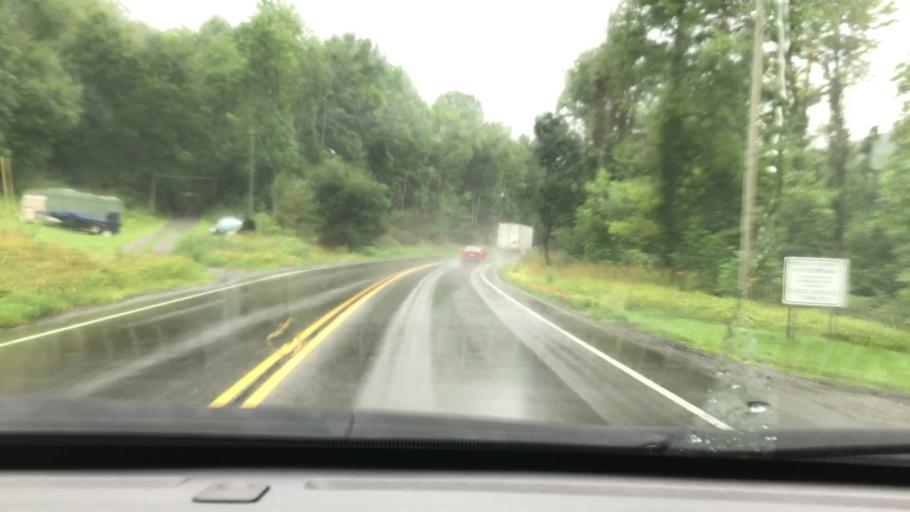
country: US
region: Pennsylvania
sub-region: Blair County
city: Tyrone
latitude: 40.7515
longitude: -78.2180
